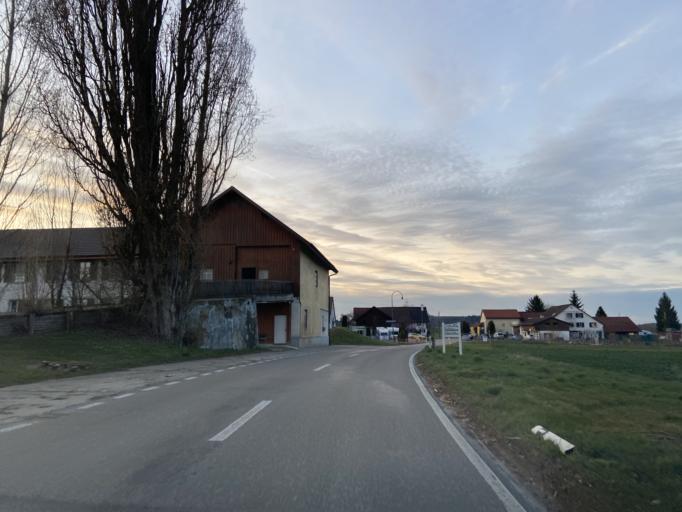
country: CH
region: Zurich
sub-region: Bezirk Winterthur
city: Wuelflingen (Kreis 6) / Lindenplatz
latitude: 47.5273
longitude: 8.6931
